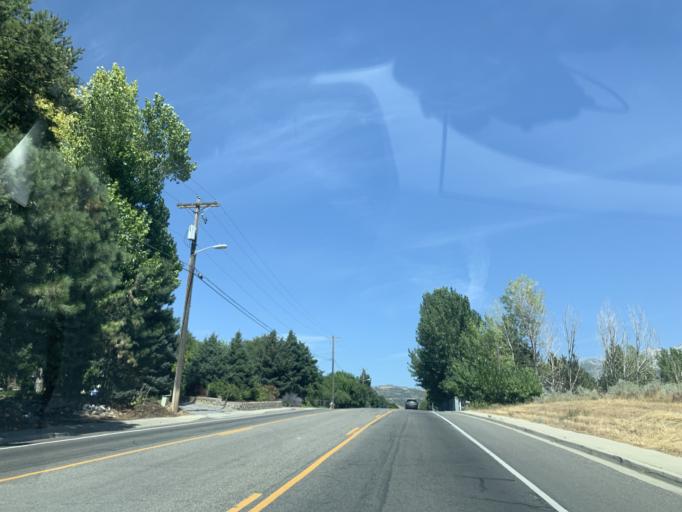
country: US
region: Utah
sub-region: Utah County
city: Lehi
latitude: 40.4086
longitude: -111.8302
